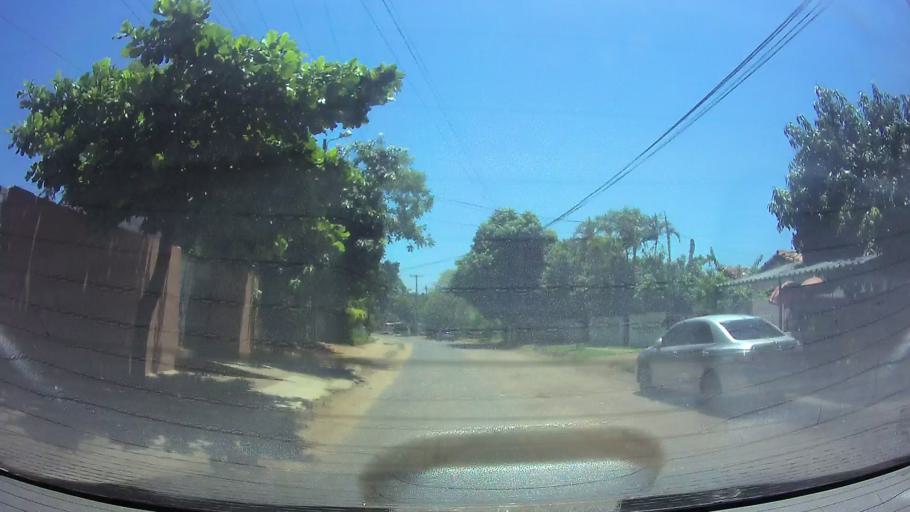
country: PY
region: Central
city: San Lorenzo
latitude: -25.3369
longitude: -57.4860
